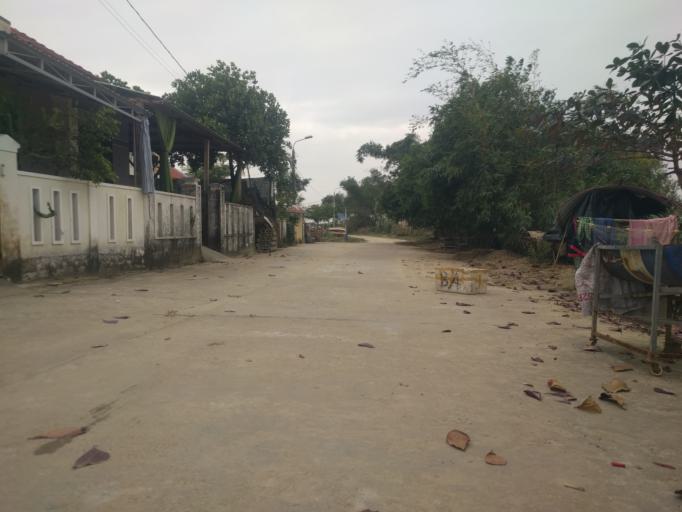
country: VN
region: Quang Nam
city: Hoi An
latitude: 15.8732
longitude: 108.3298
